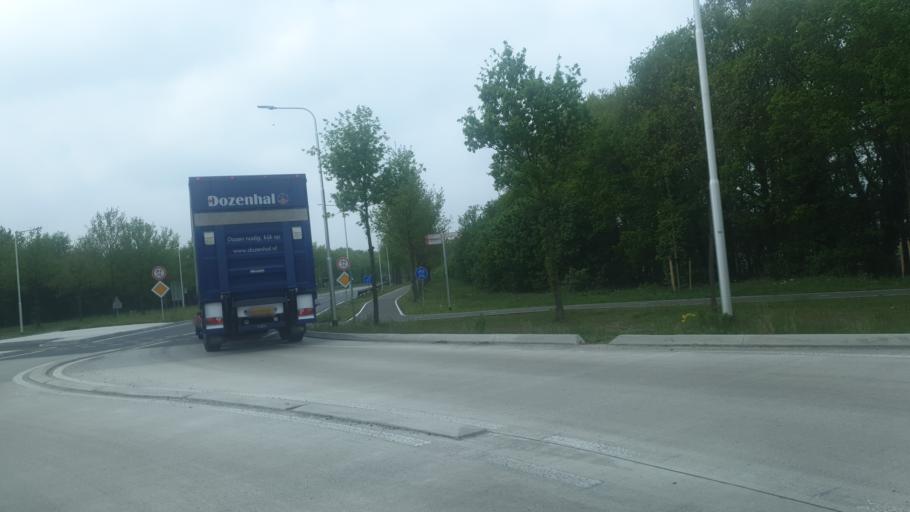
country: NL
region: North Brabant
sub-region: Gemeente Landerd
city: Reek
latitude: 51.7373
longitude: 5.6699
